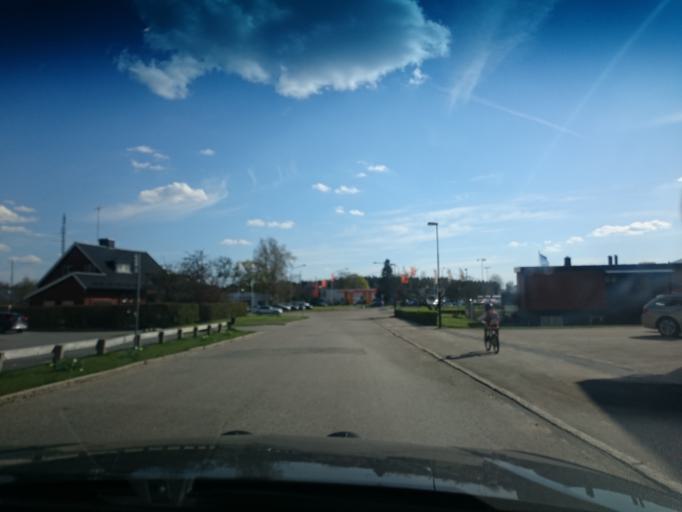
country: SE
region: Joenkoeping
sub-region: Vetlanda Kommun
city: Vetlanda
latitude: 57.4263
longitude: 15.0978
